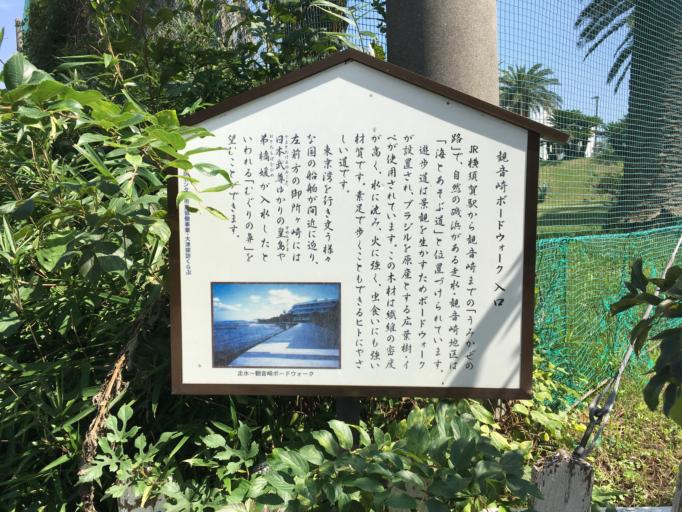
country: JP
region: Kanagawa
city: Yokosuka
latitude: 35.2613
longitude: 139.7359
